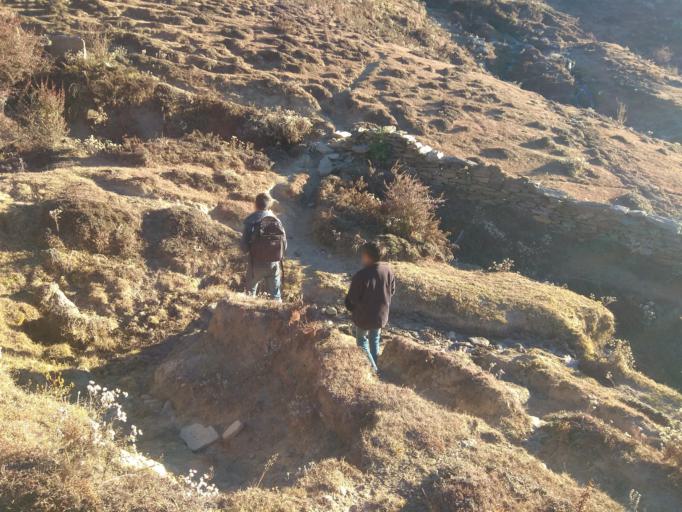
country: NP
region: Far Western
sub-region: Seti Zone
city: Achham
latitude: 29.2753
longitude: 81.6459
